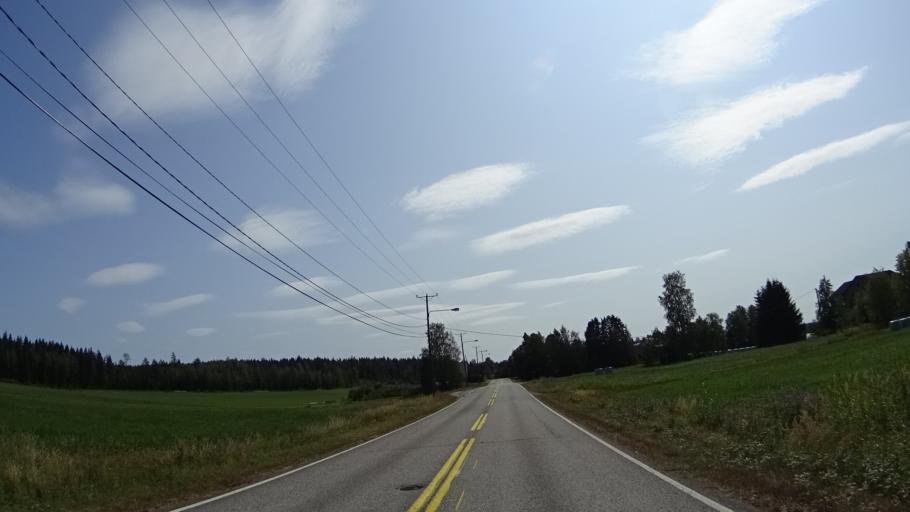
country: FI
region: Pirkanmaa
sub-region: Ylae-Pirkanmaa
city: Maenttae
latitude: 61.9116
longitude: 24.7805
